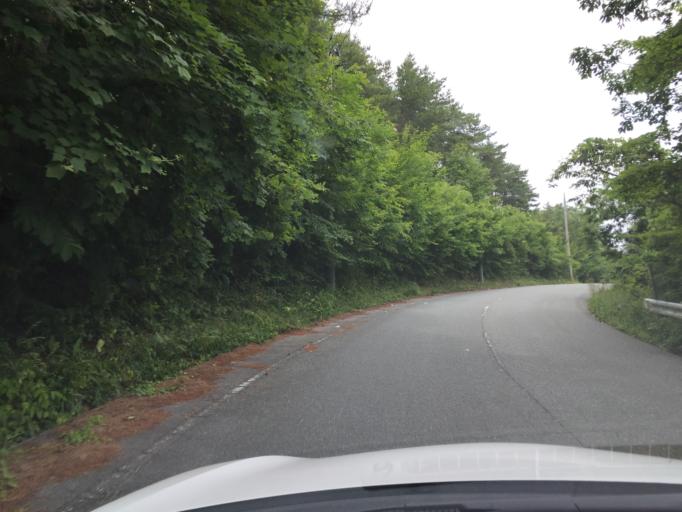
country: JP
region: Fukushima
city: Iwaki
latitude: 37.1572
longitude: 140.7007
